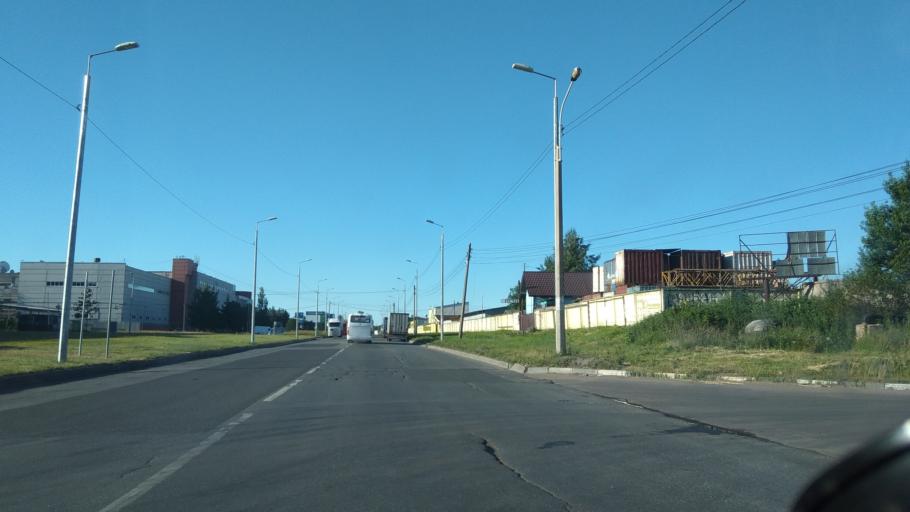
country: RU
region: Leningrad
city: Bugry
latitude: 60.0701
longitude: 30.3722
